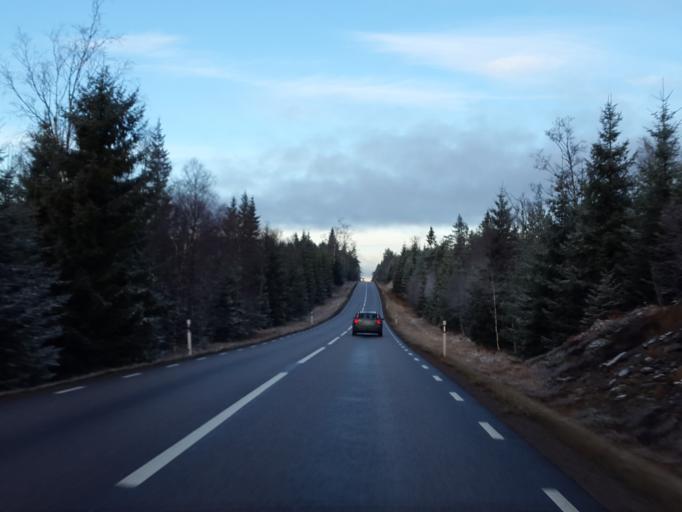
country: SE
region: Vaestra Goetaland
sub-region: Boras Kommun
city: Sjomarken
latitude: 57.7557
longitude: 12.8546
